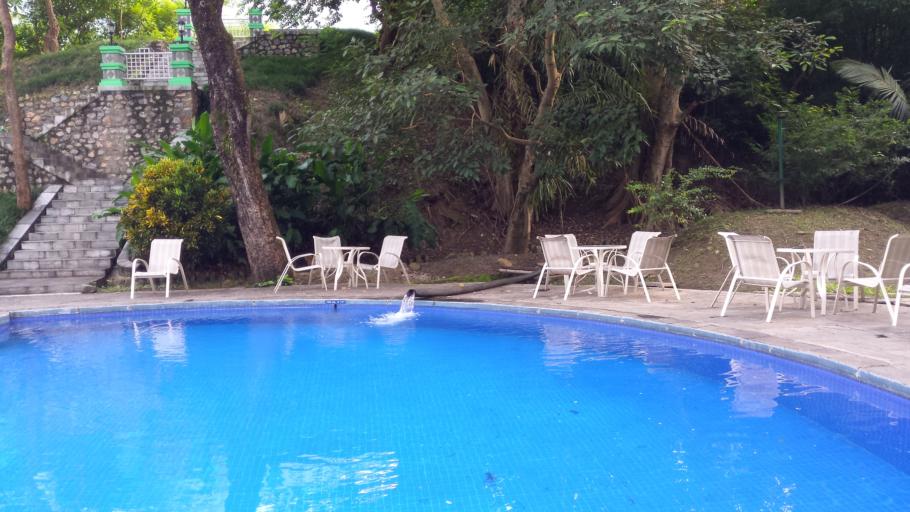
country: NP
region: Central Region
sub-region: Narayani Zone
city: Bharatpur
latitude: 27.8749
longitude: 84.6162
